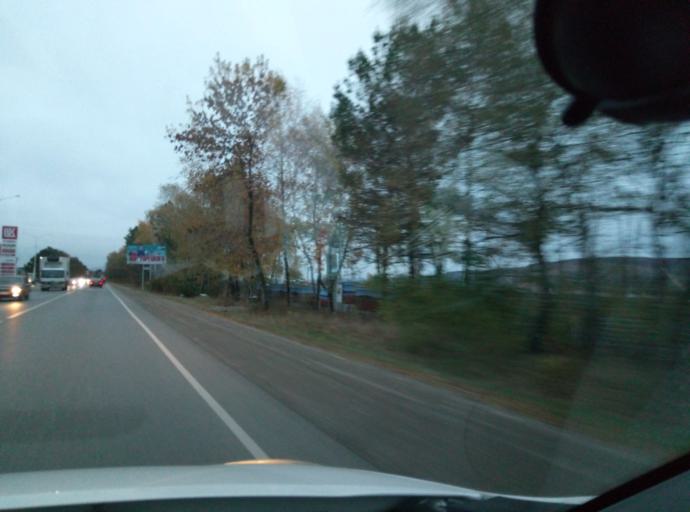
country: RU
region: Stavropol'skiy
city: Vinsady
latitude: 44.0546
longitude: 42.9247
